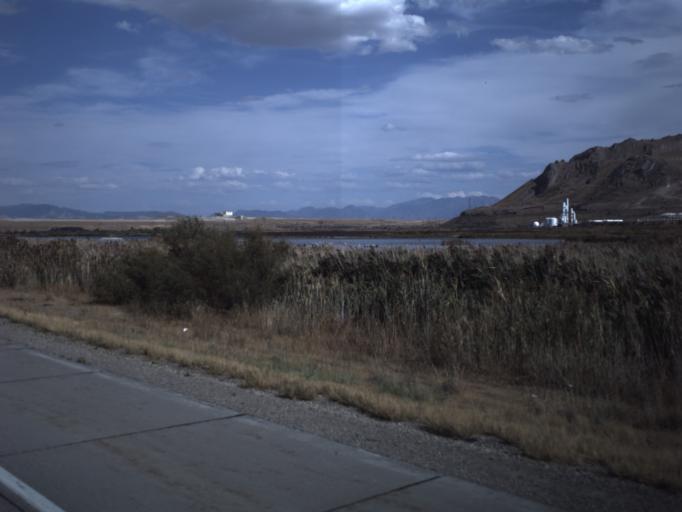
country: US
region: Utah
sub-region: Salt Lake County
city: Magna
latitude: 40.7312
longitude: -112.2059
